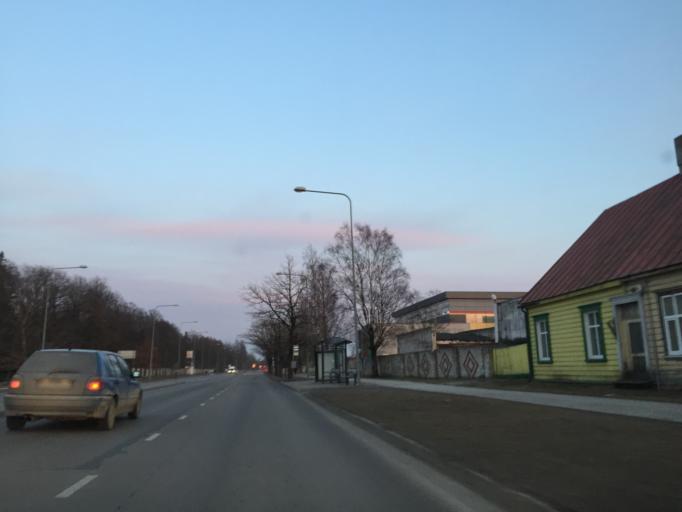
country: EE
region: Paernumaa
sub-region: Paernu linn
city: Parnu
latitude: 58.3779
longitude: 24.5310
